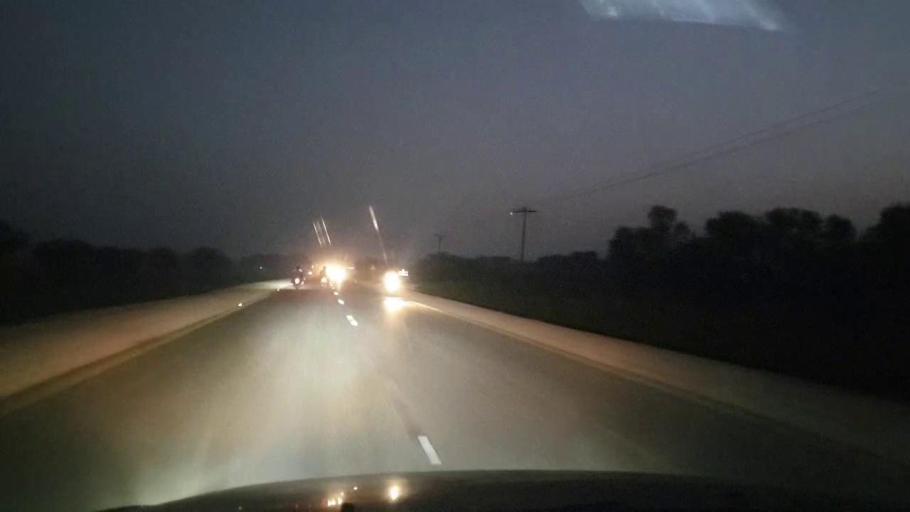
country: PK
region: Sindh
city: Chambar
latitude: 25.3185
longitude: 68.8033
